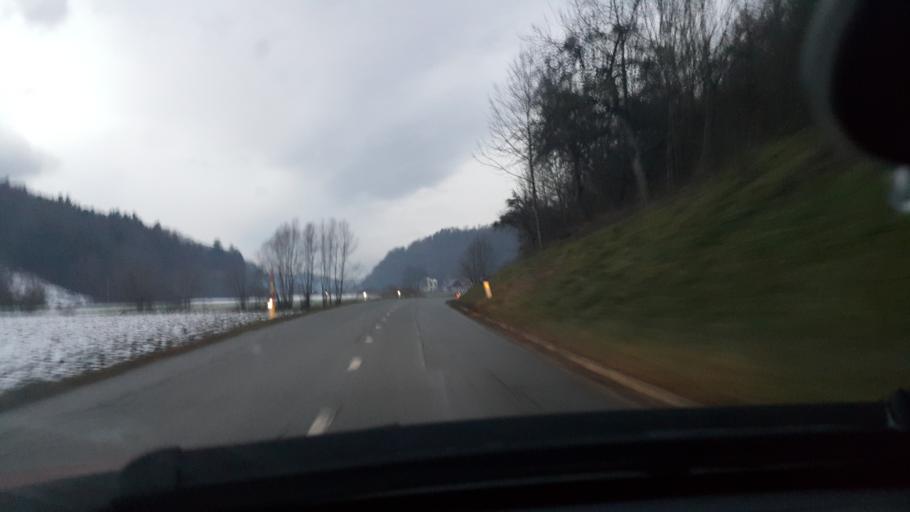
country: SI
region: Kungota
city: Zgornja Kungota
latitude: 46.6370
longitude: 15.6101
